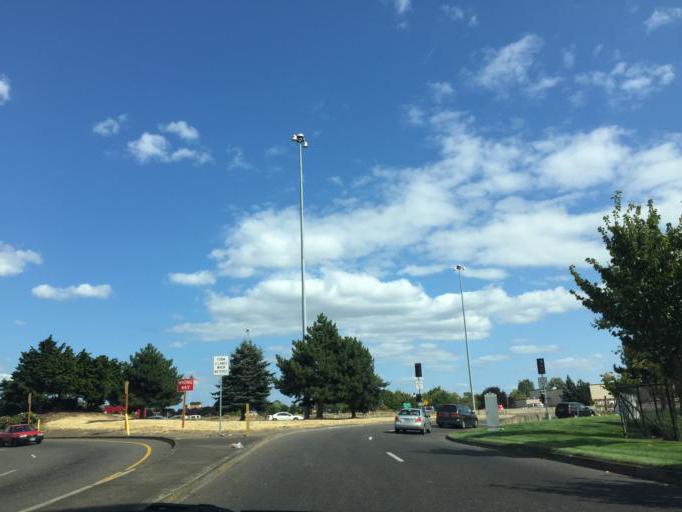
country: US
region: Washington
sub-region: Clark County
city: Vancouver
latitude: 45.6117
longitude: -122.6804
